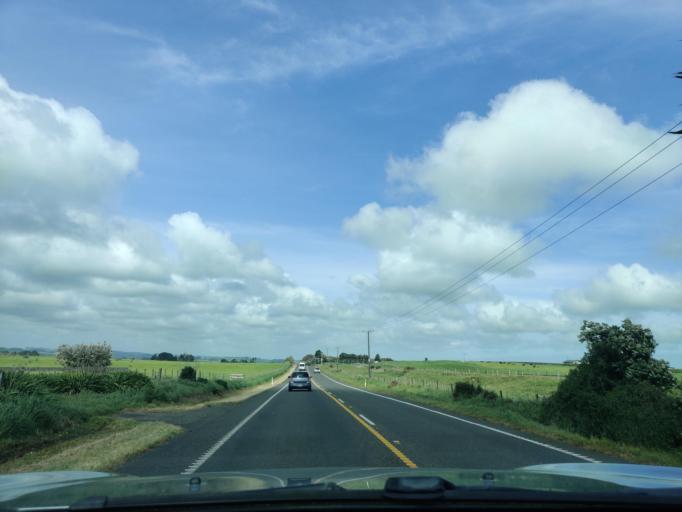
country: NZ
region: Taranaki
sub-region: South Taranaki District
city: Patea
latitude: -39.7751
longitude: 174.6790
